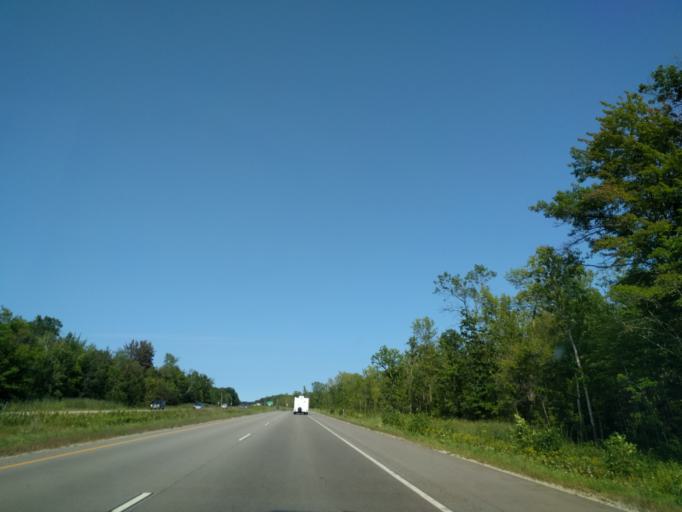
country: US
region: Wisconsin
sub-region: Oconto County
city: Oconto
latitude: 44.8315
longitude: -87.9235
